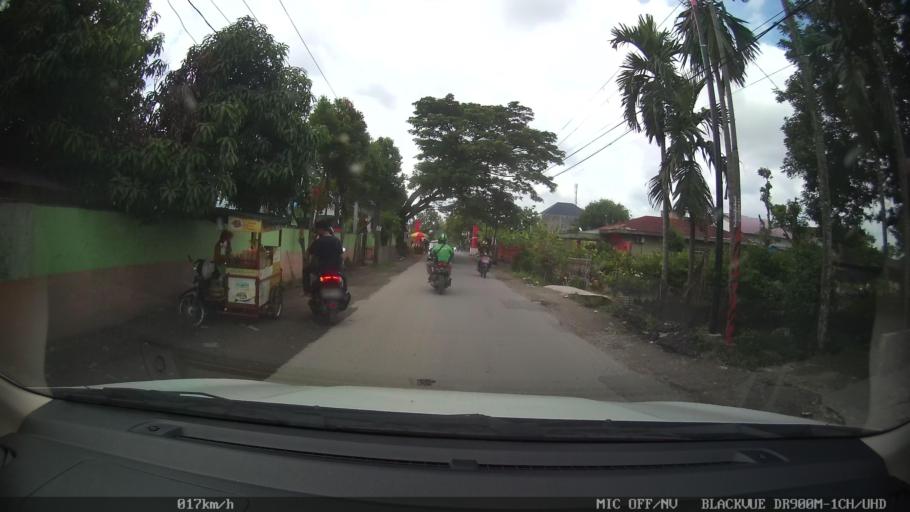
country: ID
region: North Sumatra
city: Medan
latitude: 3.6178
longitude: 98.7294
